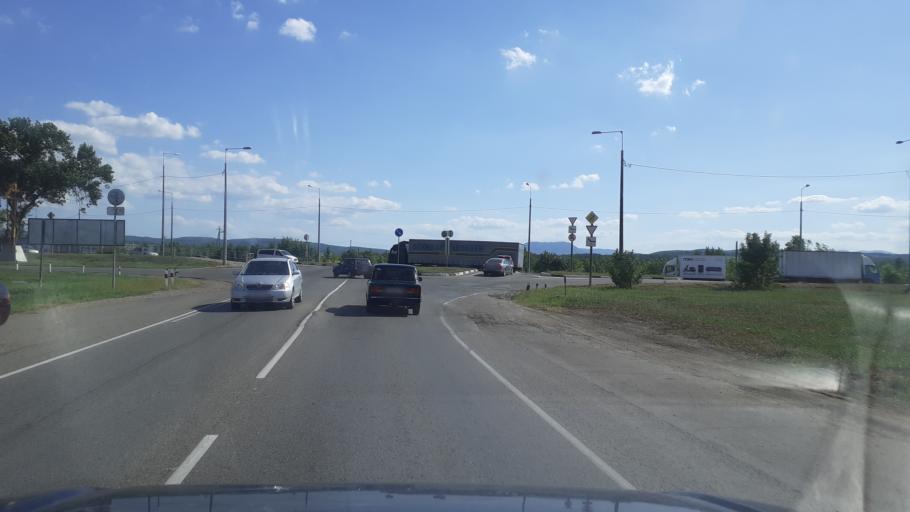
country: RU
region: Krasnodarskiy
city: Severskaya
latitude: 44.8441
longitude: 38.6571
